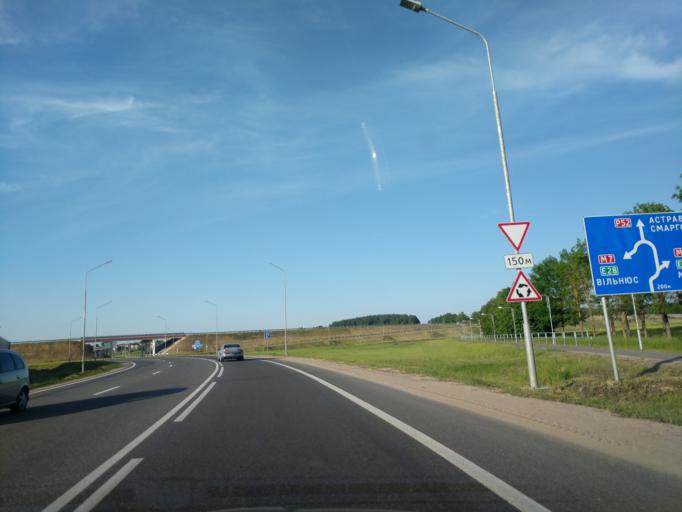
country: BY
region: Grodnenskaya
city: Ashmyany
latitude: 54.4339
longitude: 25.9648
